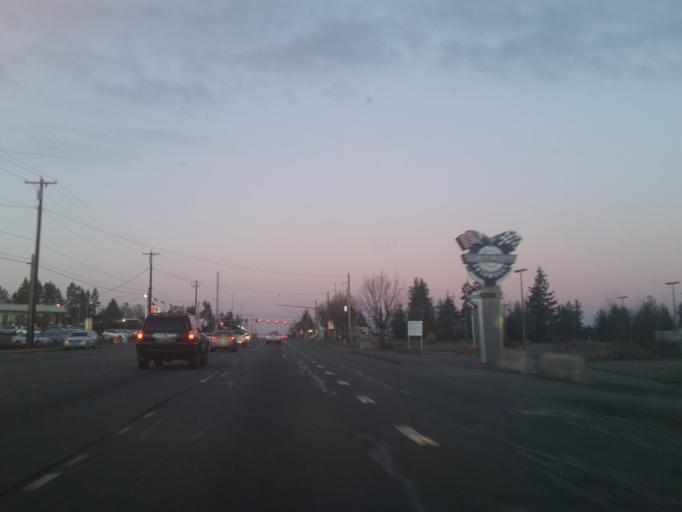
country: US
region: Washington
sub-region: Snohomish County
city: Lynnwood
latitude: 47.8045
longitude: -122.3281
